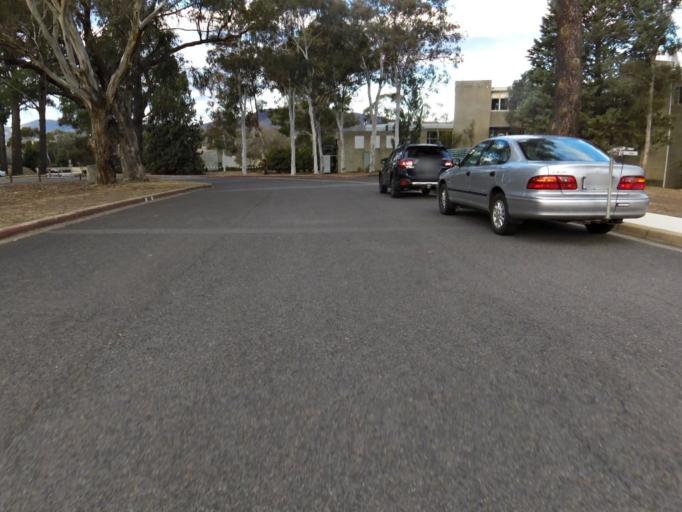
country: AU
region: Australian Capital Territory
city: Acton
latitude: -35.2712
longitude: 149.1118
